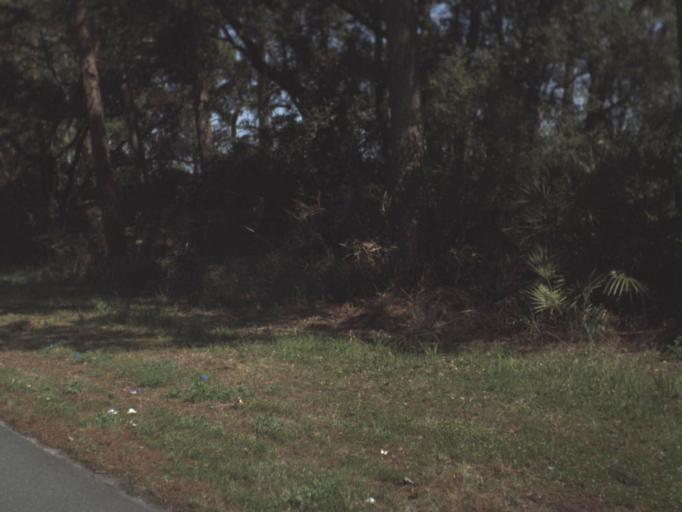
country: US
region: Florida
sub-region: Franklin County
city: Carrabelle
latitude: 29.8566
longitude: -84.6336
